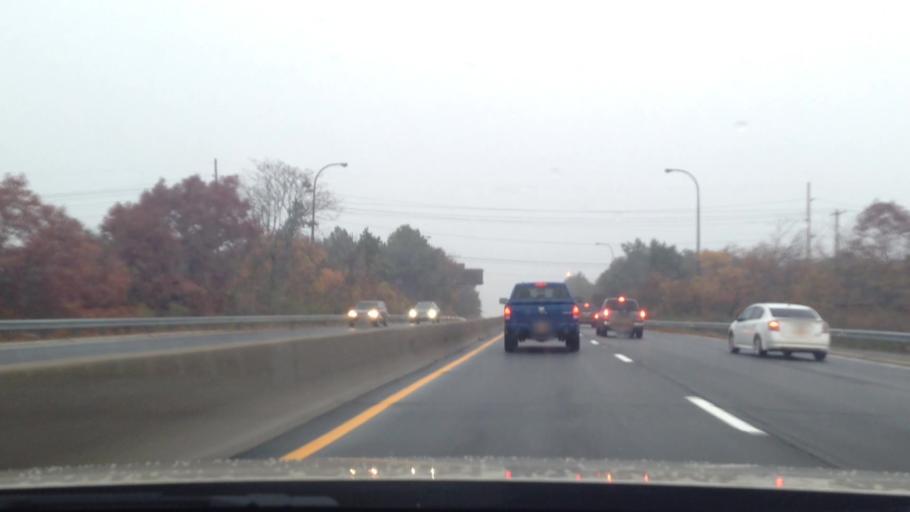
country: US
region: New York
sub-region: Suffolk County
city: Bay Wood
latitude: 40.7709
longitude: -73.2798
